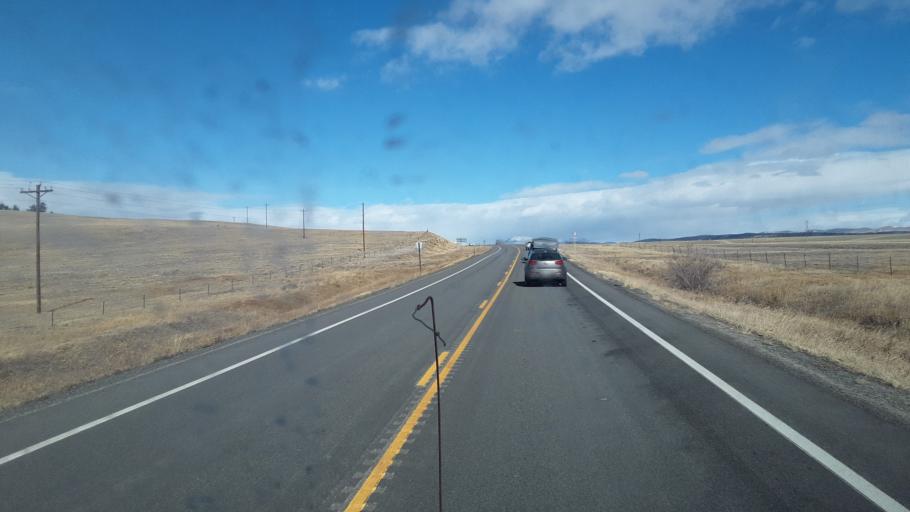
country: US
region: Colorado
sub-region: Park County
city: Fairplay
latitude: 39.0734
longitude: -105.9741
